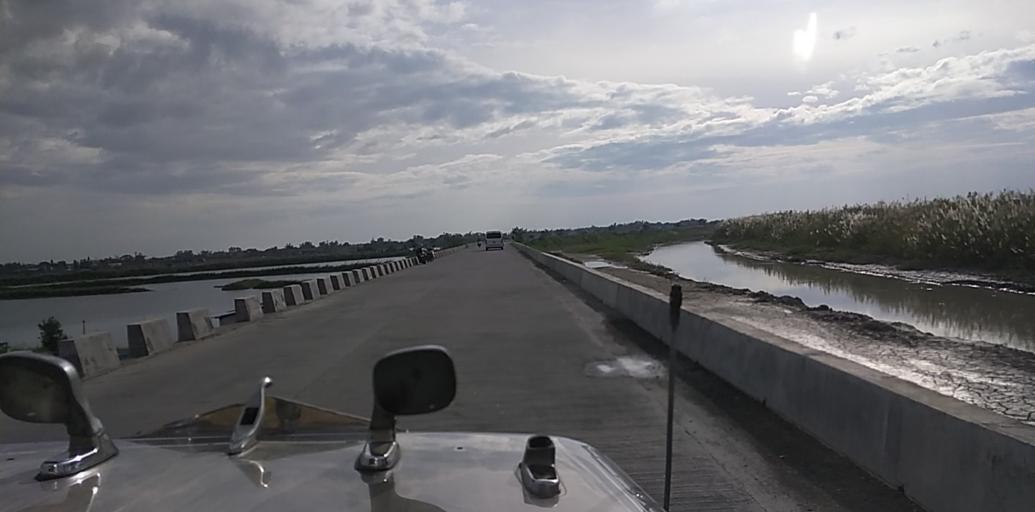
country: PH
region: Central Luzon
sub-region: Province of Pampanga
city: Minalin
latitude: 14.9725
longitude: 120.6786
